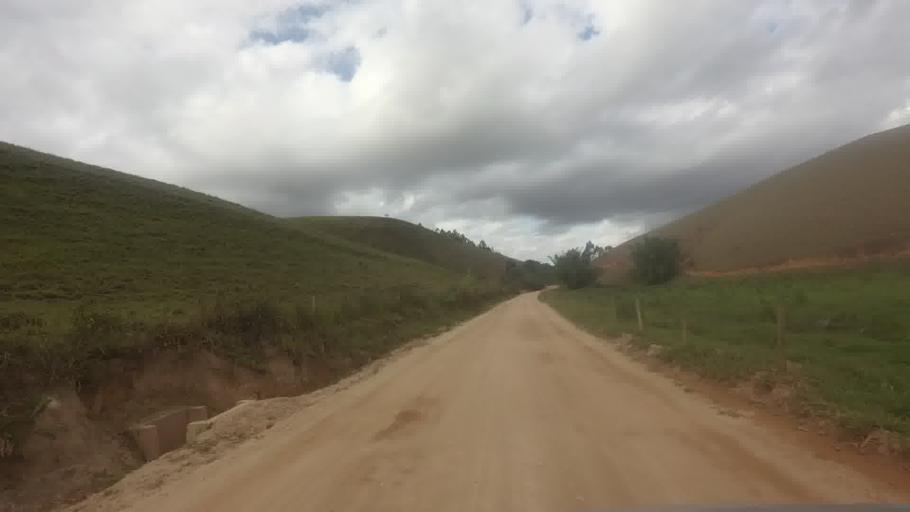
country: BR
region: Espirito Santo
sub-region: Mimoso Do Sul
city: Mimoso do Sul
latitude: -20.9609
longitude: -41.4438
